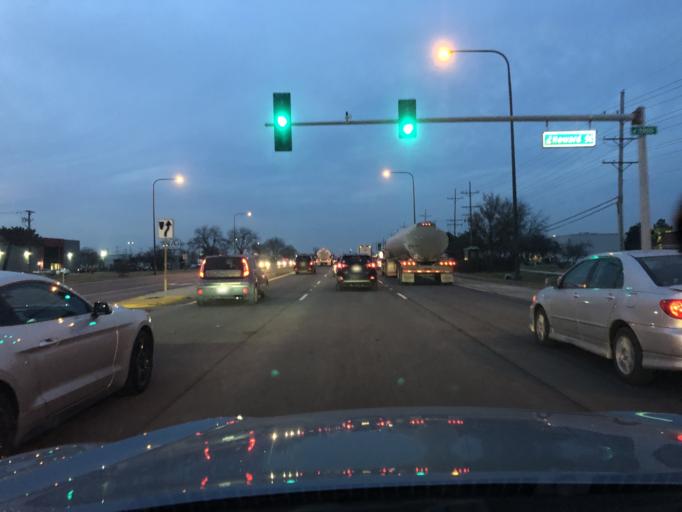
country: US
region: Illinois
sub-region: Cook County
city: Elk Grove Village
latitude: 42.0160
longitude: -87.9597
